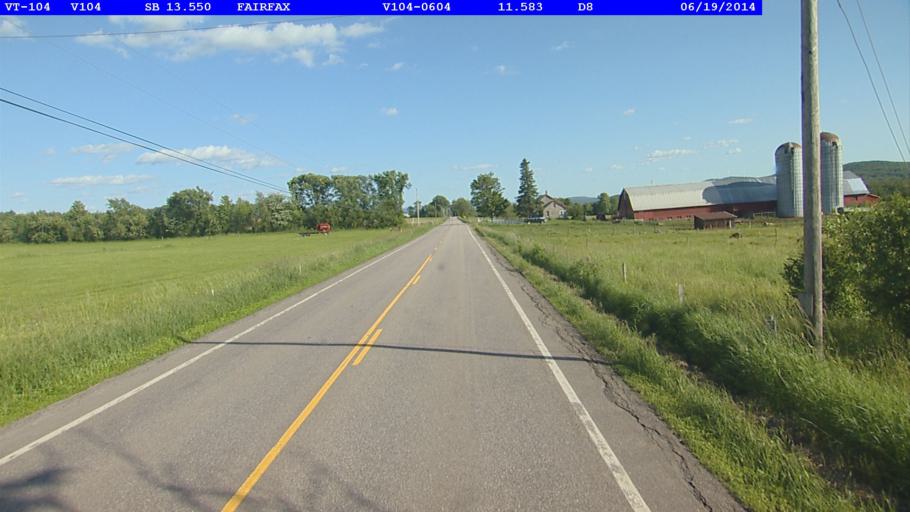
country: US
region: Vermont
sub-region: Franklin County
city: Saint Albans
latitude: 44.7507
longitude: -73.0539
